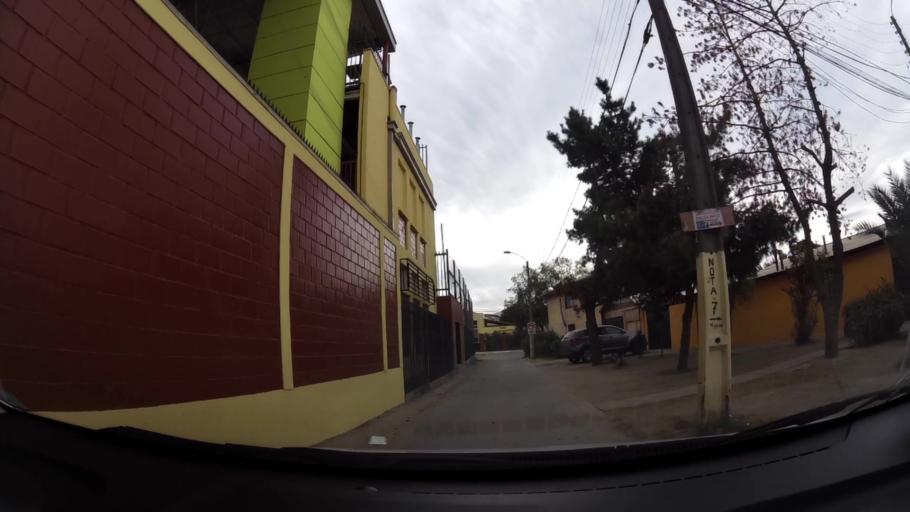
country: CL
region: O'Higgins
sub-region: Provincia de Cachapoal
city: Rancagua
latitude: -34.1528
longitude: -70.7293
